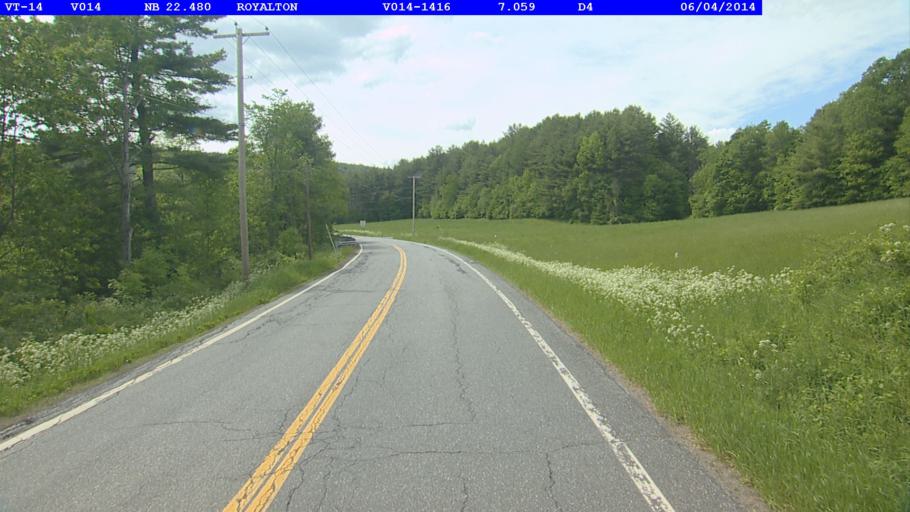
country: US
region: Vermont
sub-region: Orange County
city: Randolph
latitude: 43.8399
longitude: -72.5799
